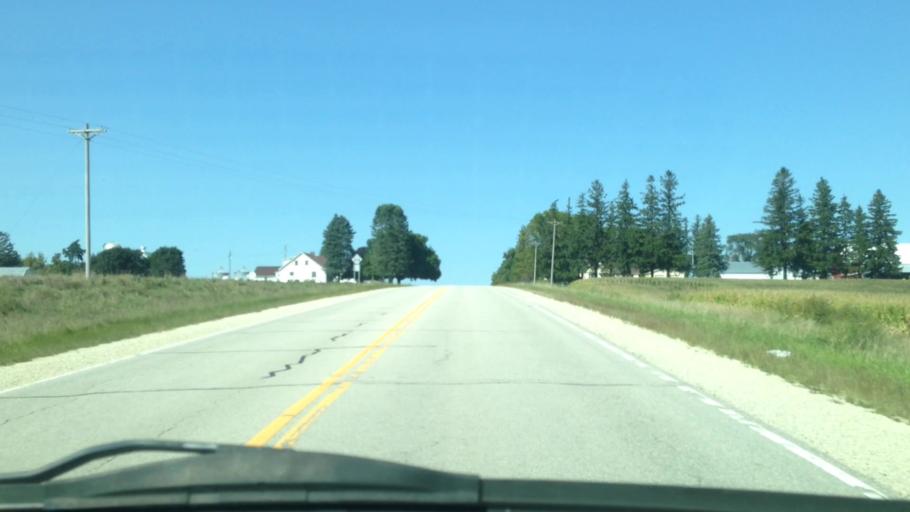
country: US
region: Minnesota
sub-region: Houston County
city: Spring Grove
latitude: 43.6058
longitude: -91.7901
